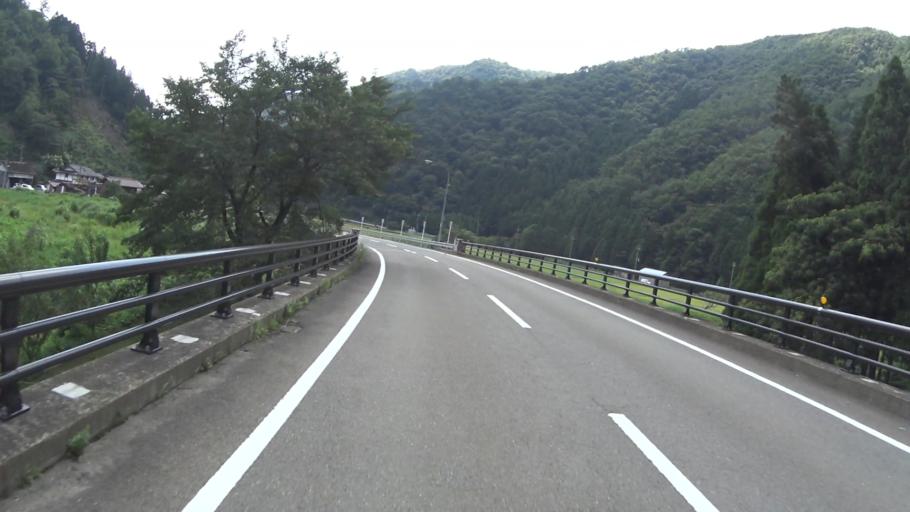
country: JP
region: Fukui
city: Obama
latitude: 35.3342
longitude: 135.5702
